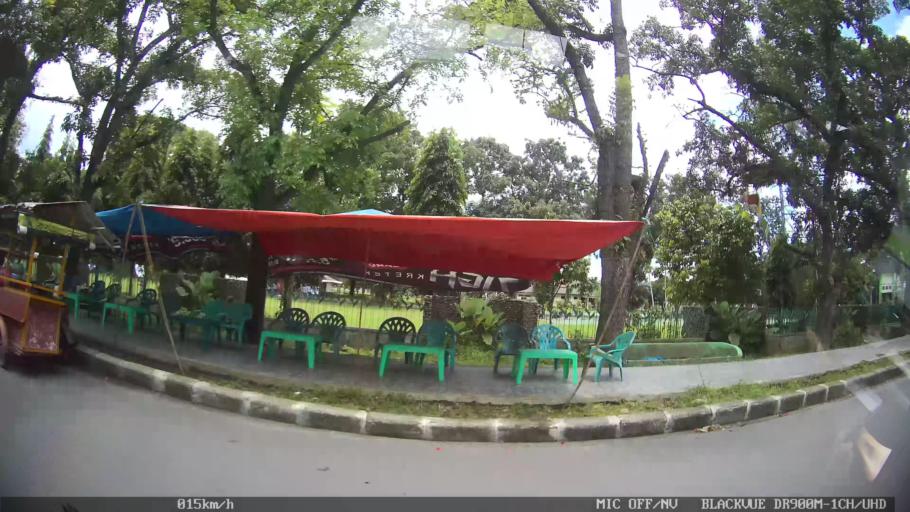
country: ID
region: North Sumatra
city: Medan
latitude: 3.6145
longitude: 98.7097
